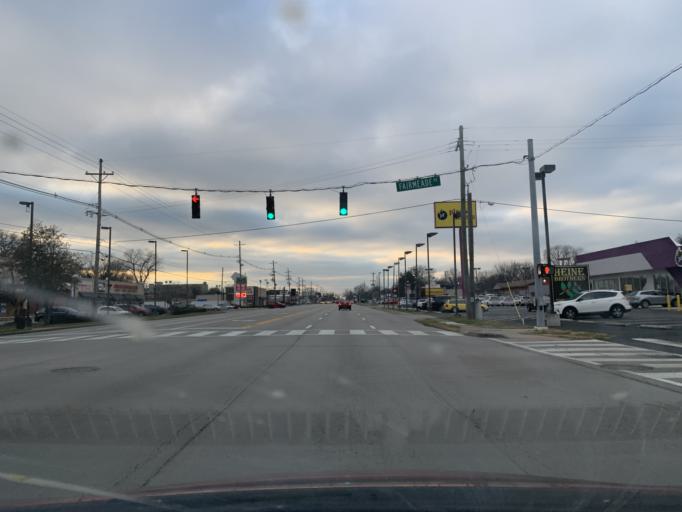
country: US
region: Kentucky
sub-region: Jefferson County
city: Beechwood Village
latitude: 38.2514
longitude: -85.6361
